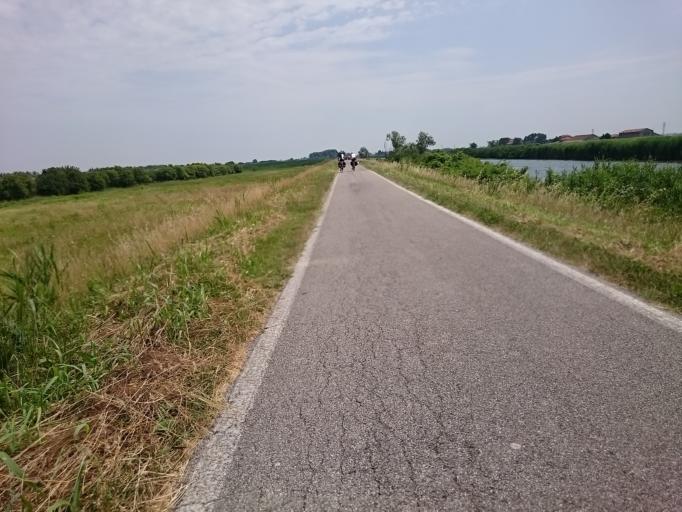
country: IT
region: Veneto
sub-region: Provincia di Venezia
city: Valli
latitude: 45.1884
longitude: 12.2224
